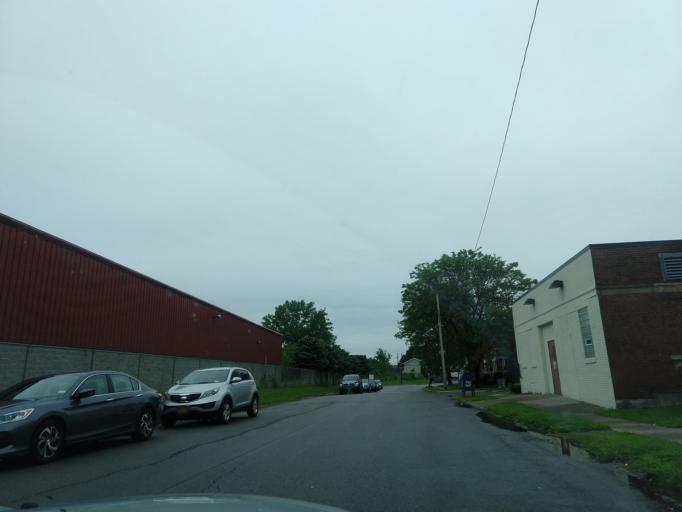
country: US
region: New York
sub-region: Erie County
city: Lackawanna
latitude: 42.8213
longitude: -78.8472
